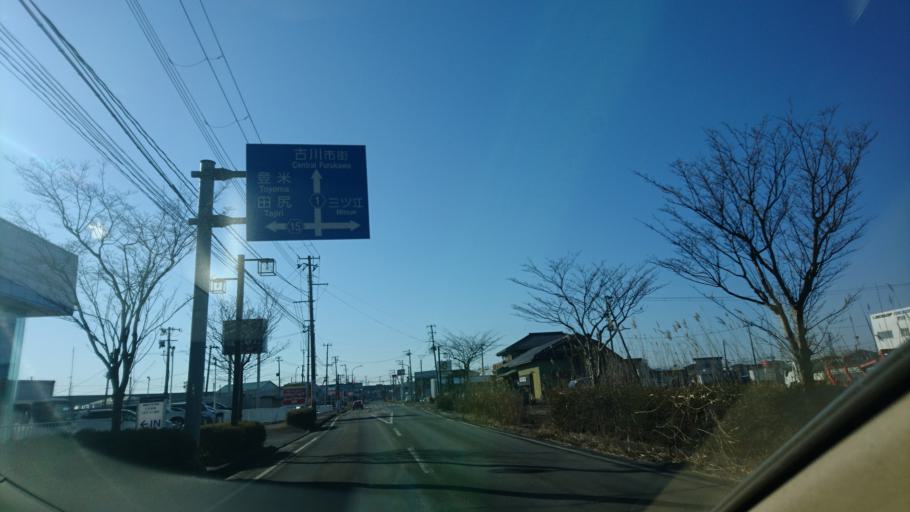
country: JP
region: Miyagi
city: Furukawa
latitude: 38.5962
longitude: 140.9765
